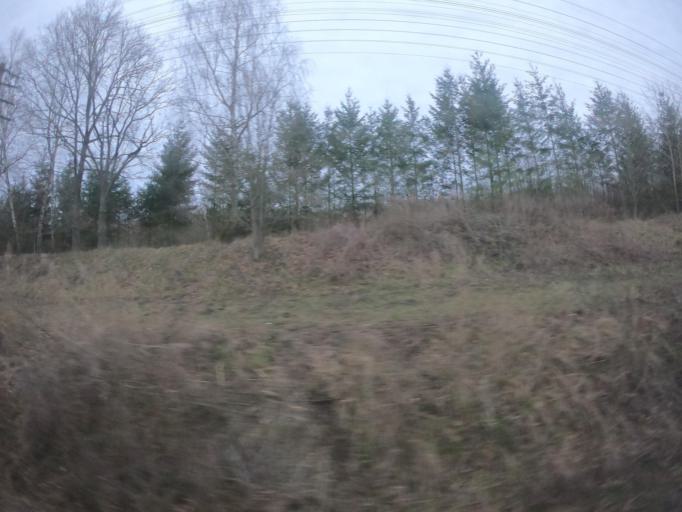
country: PL
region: West Pomeranian Voivodeship
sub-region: Powiat szczecinecki
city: Borne Sulinowo
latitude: 53.6544
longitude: 16.5877
